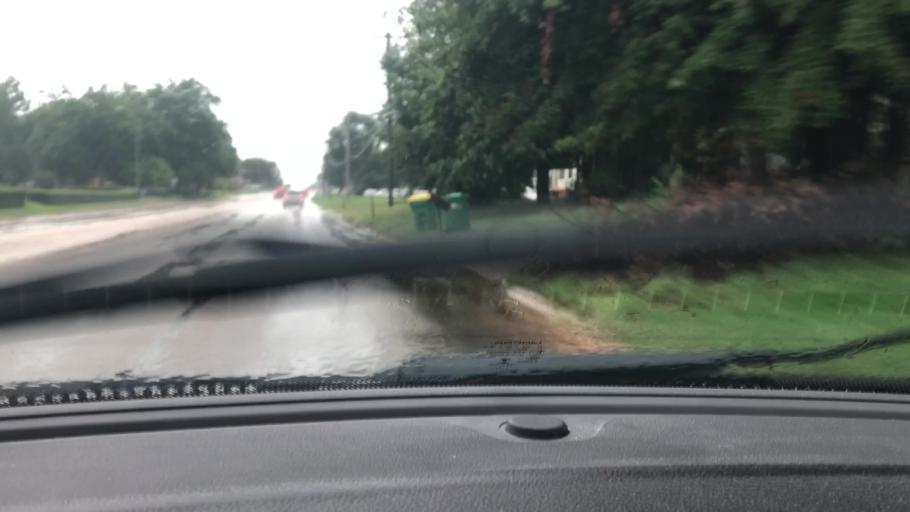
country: US
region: Texas
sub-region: Bowie County
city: Wake Village
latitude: 33.4432
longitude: -94.0804
